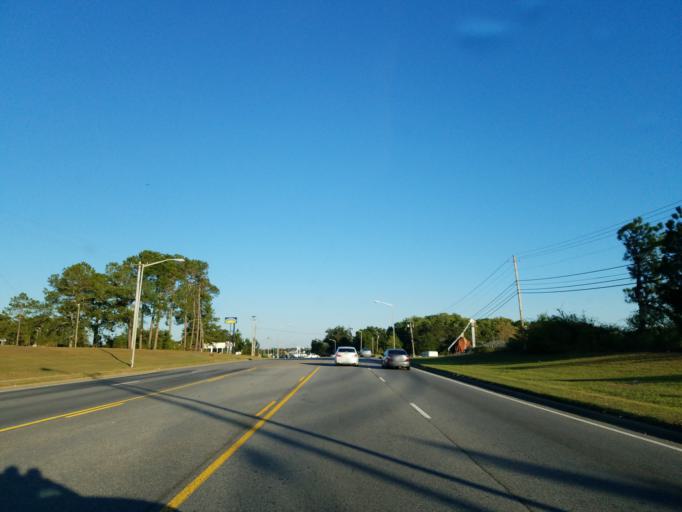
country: US
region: Georgia
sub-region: Worth County
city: Sylvester
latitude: 31.5283
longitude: -83.8212
